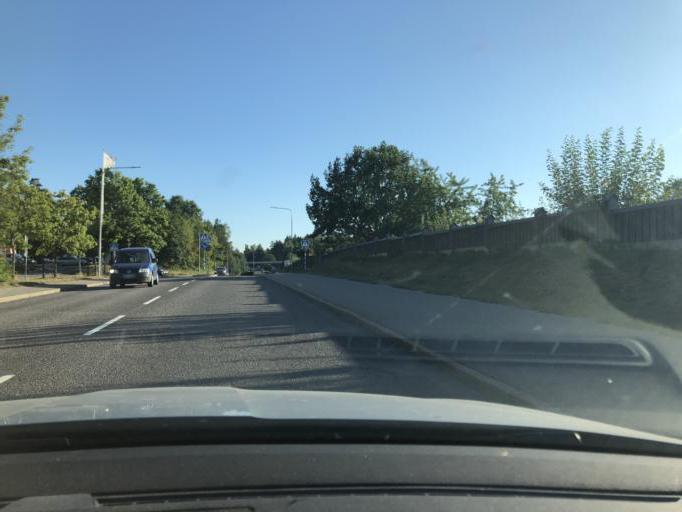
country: SE
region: Stockholm
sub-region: Sodertalje Kommun
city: Soedertaelje
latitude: 59.1812
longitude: 17.6163
